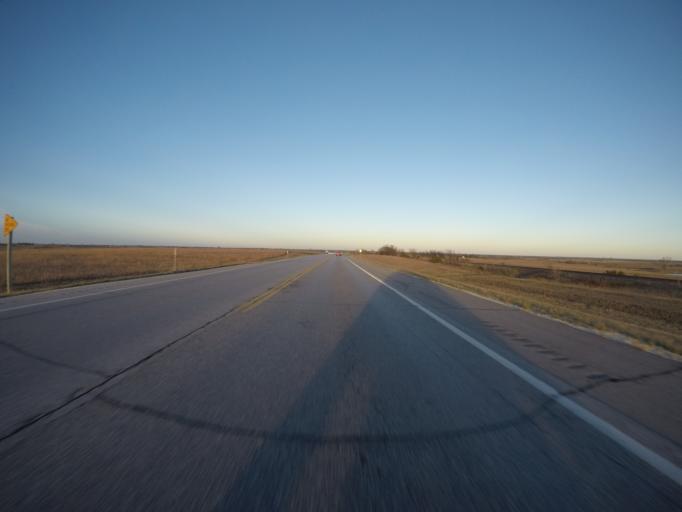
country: US
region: Kansas
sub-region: Marion County
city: Peabody
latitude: 38.1479
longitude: -97.2234
